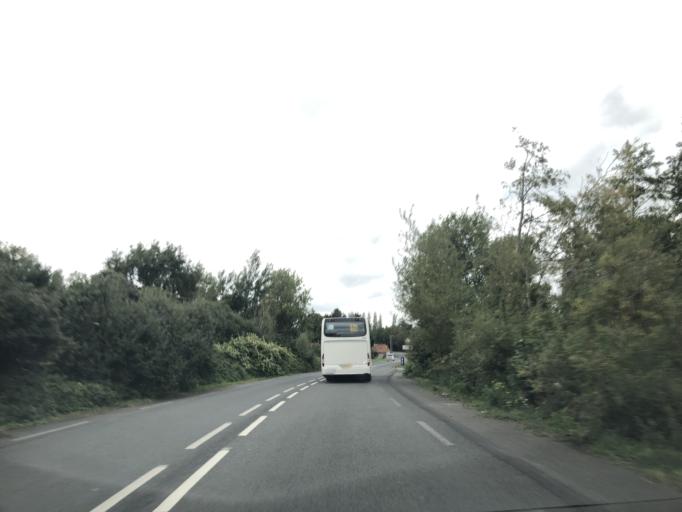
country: FR
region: Nord-Pas-de-Calais
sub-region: Departement du Pas-de-Calais
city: Rang-du-Fliers
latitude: 50.4335
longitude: 1.6511
